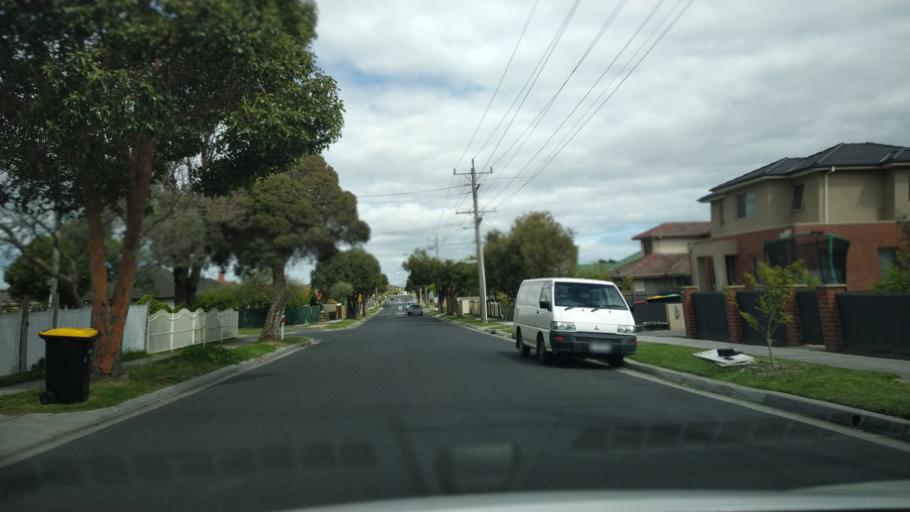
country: AU
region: Victoria
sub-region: Greater Dandenong
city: Noble Park
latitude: -37.9746
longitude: 145.1729
